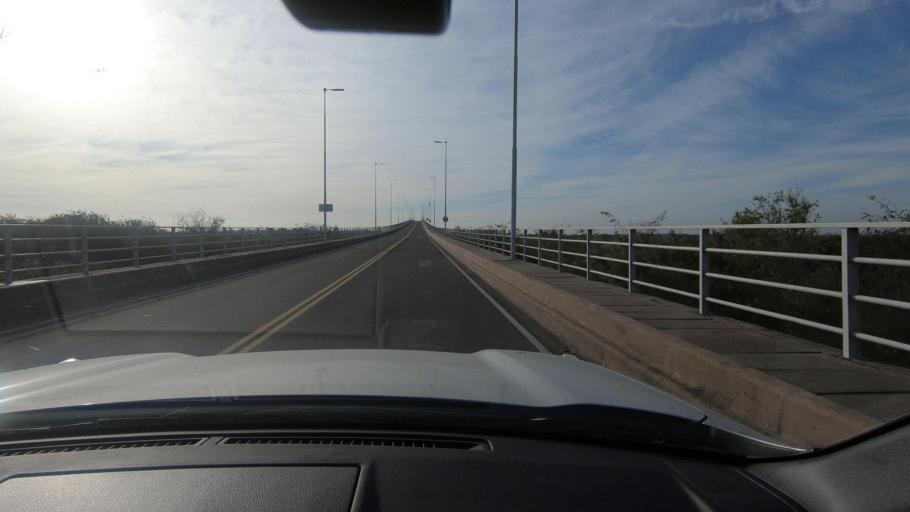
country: AR
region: Entre Rios
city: Colon
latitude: -32.2384
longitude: -58.1579
